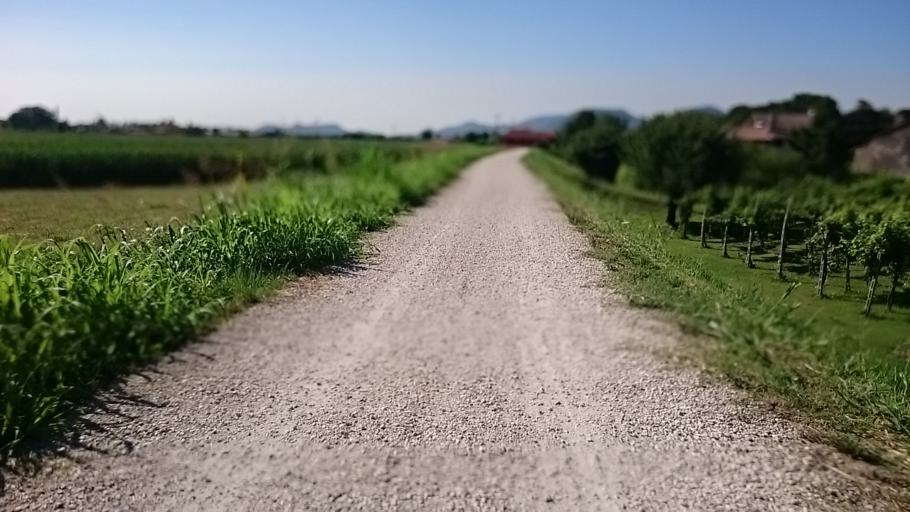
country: IT
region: Veneto
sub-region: Provincia di Vicenza
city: Montegaldella
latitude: 45.4459
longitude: 11.6586
